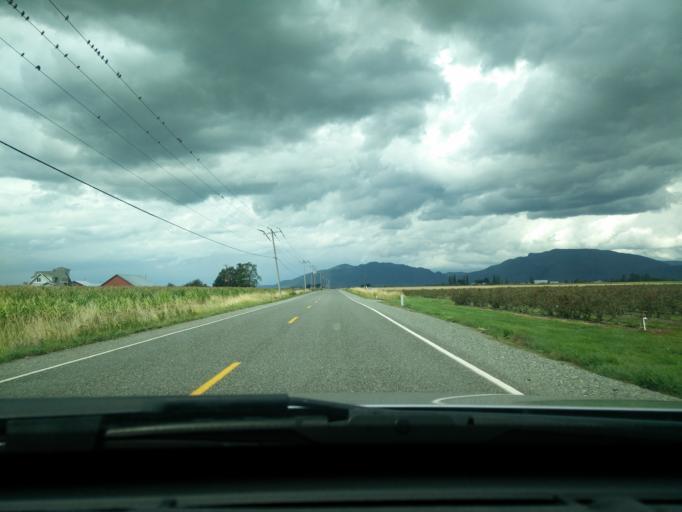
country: US
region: Washington
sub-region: Skagit County
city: Anacortes
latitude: 48.5248
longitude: -122.4720
